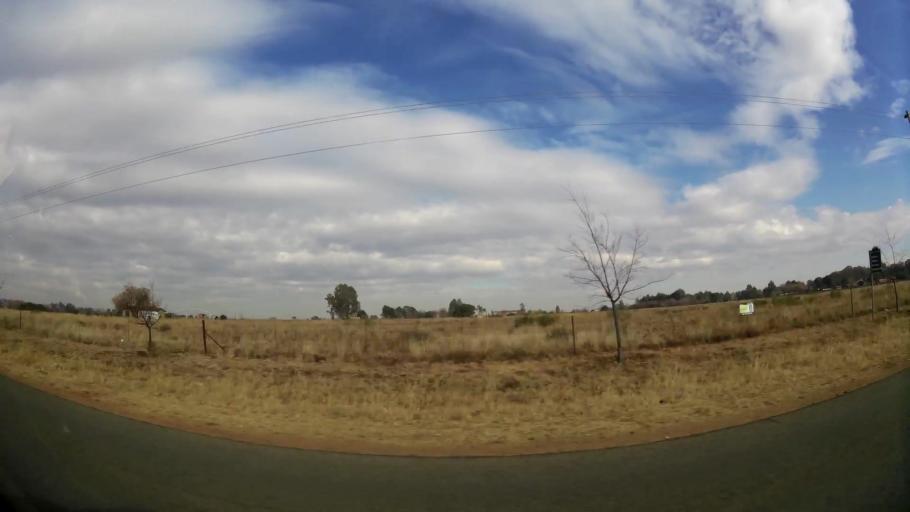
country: ZA
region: Gauteng
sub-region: Sedibeng District Municipality
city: Meyerton
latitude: -26.5542
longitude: 28.0614
